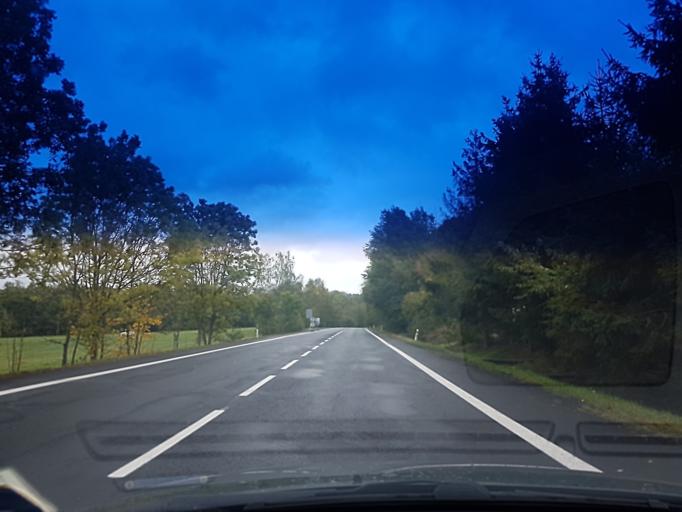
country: CZ
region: Karlovarsky
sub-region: Okres Cheb
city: Cheb
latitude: 50.0811
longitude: 12.3317
